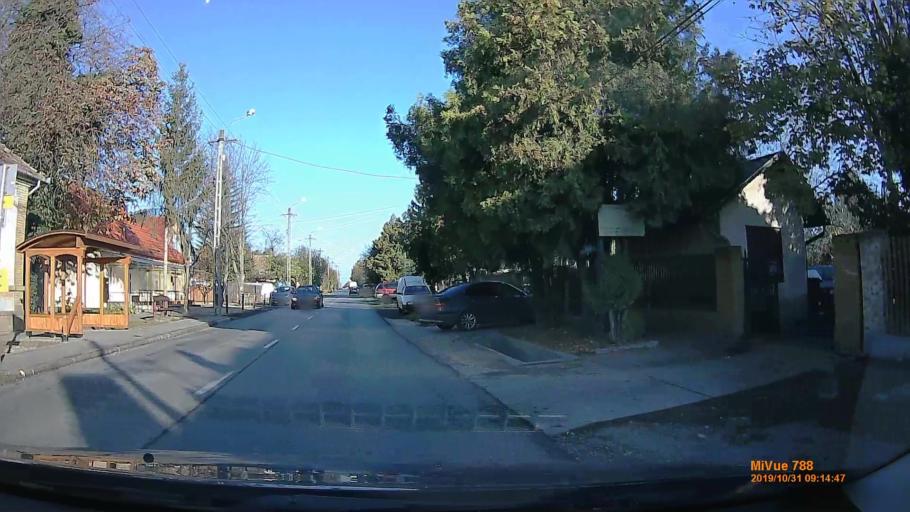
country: HU
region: Pest
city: Peteri
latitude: 47.3887
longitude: 19.4098
